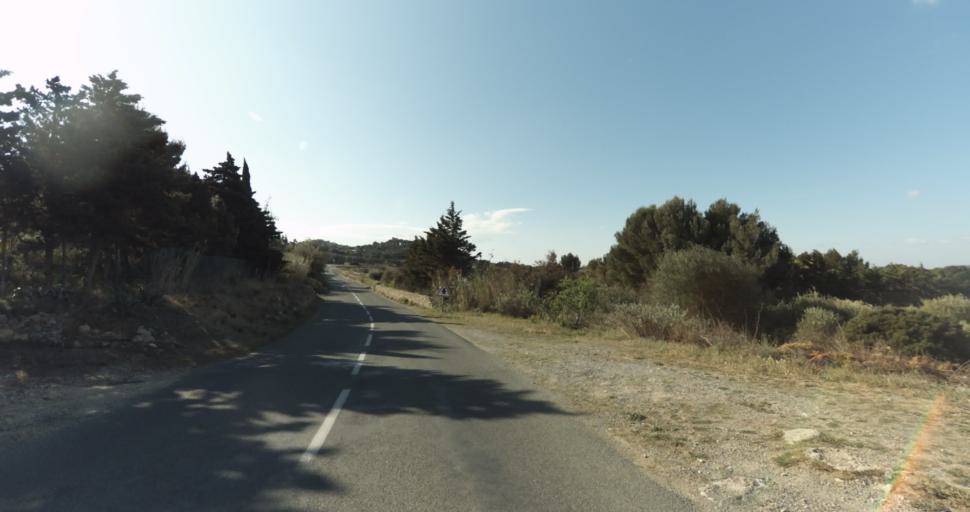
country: FR
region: Languedoc-Roussillon
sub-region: Departement de l'Aude
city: Leucate
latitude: 42.9152
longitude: 3.0188
